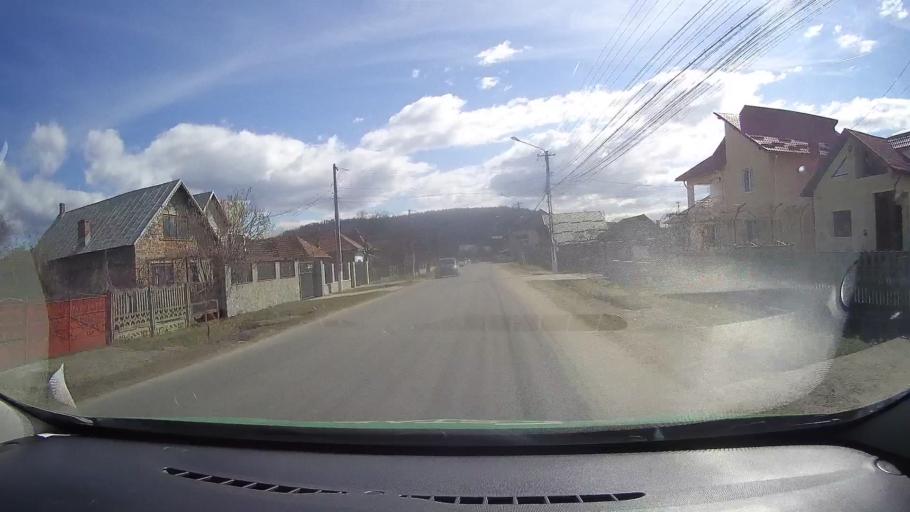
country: RO
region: Dambovita
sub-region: Comuna Vulcana-Pandele
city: Gura Vulcanei
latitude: 45.0220
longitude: 25.3974
